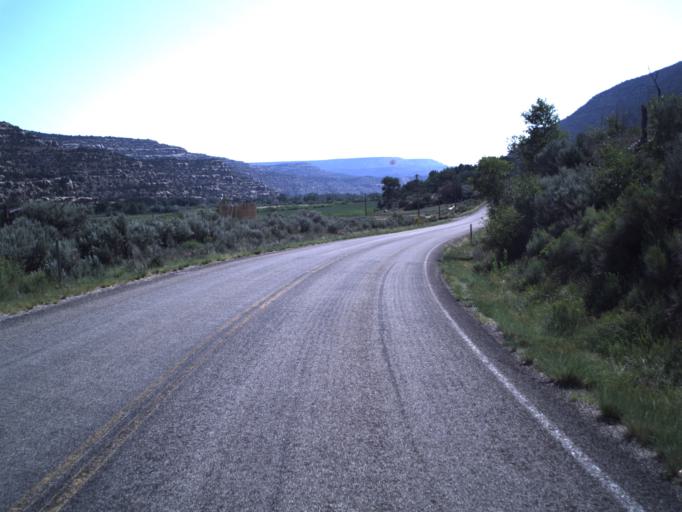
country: US
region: Utah
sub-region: Duchesne County
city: Duchesne
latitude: 40.2966
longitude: -110.5702
